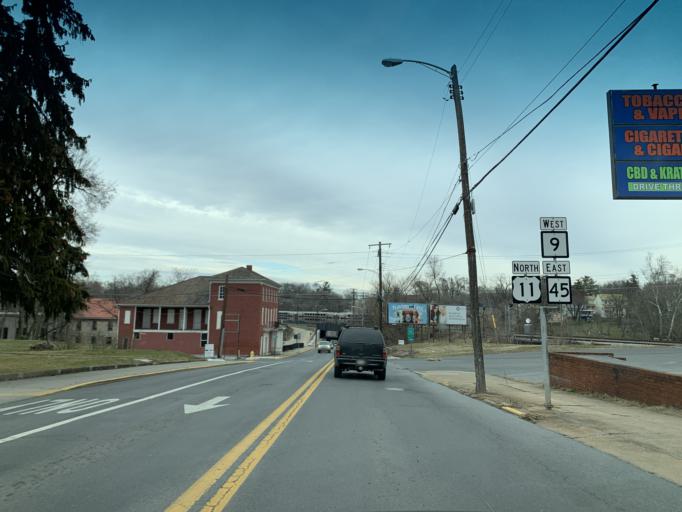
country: US
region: West Virginia
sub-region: Berkeley County
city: Martinsburg
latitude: 39.4602
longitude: -77.9627
